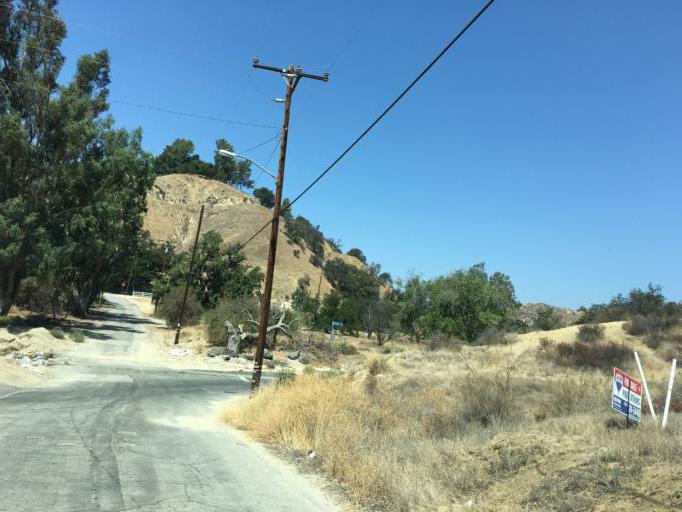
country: US
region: California
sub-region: Los Angeles County
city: Val Verde
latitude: 34.4432
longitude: -118.6555
